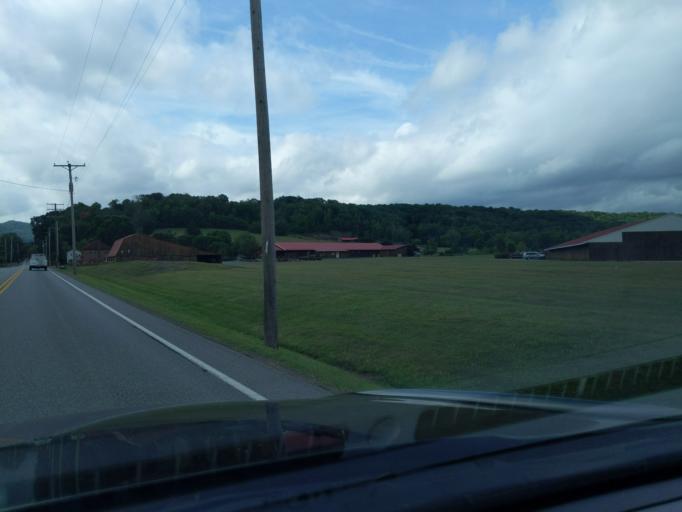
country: US
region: Pennsylvania
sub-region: Blair County
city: Duncansville
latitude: 40.3891
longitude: -78.4128
